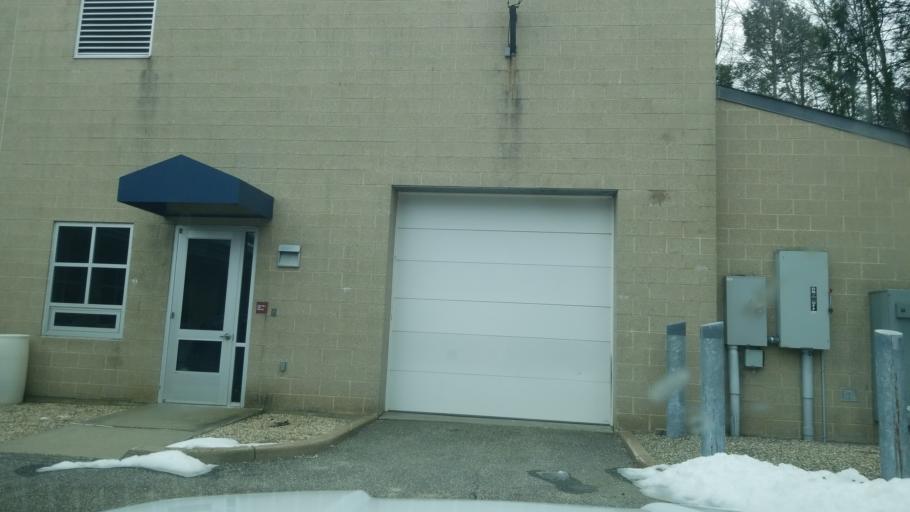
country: US
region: Connecticut
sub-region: Litchfield County
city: West Torrington
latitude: 41.8399
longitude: -73.1607
